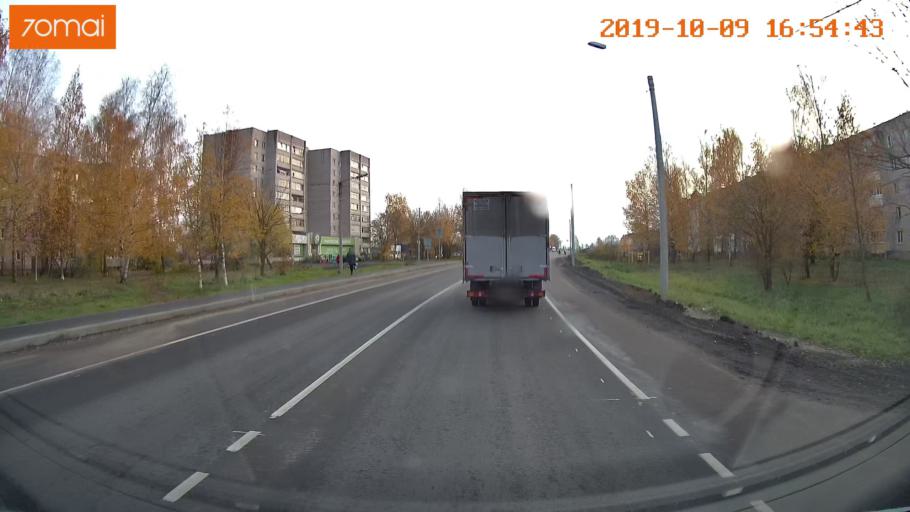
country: RU
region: Ivanovo
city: Privolzhsk
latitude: 57.3719
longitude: 41.2784
